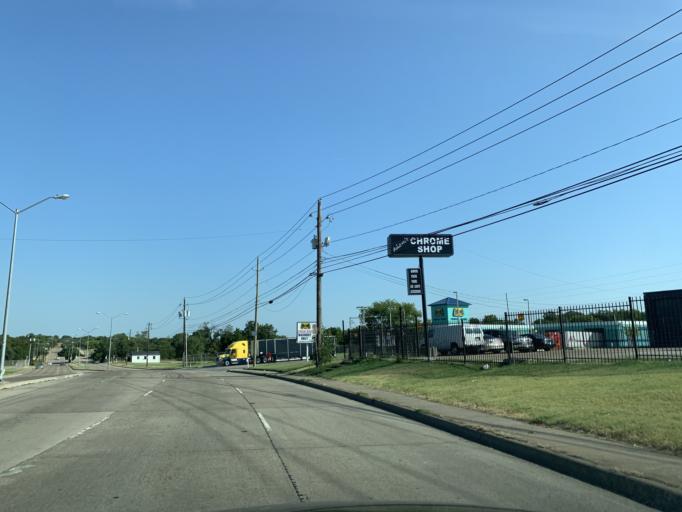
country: US
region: Texas
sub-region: Dallas County
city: Hutchins
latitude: 32.6571
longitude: -96.7504
